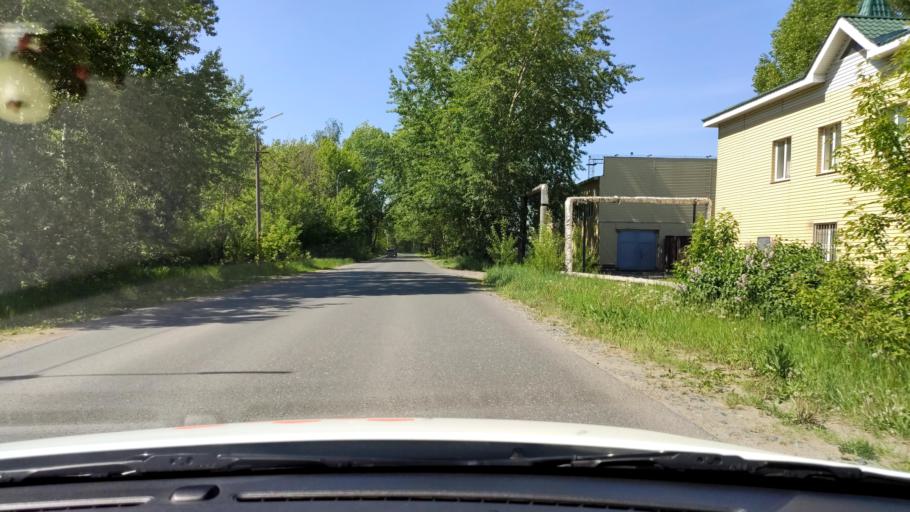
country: RU
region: Tatarstan
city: Osinovo
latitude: 55.8184
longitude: 48.8635
